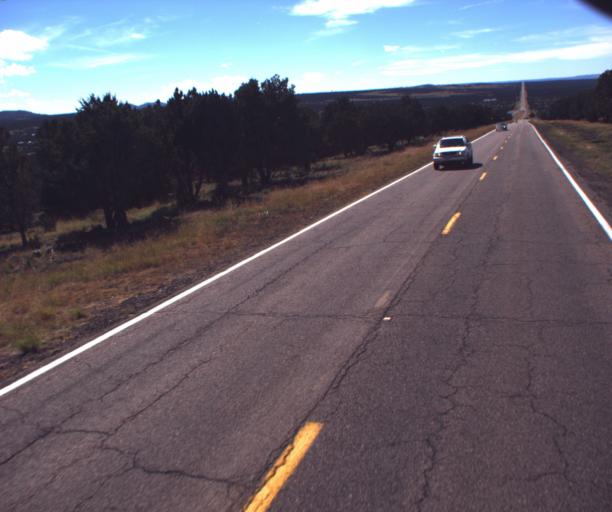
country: US
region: Arizona
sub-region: Navajo County
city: White Mountain Lake
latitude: 34.2885
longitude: -109.8223
